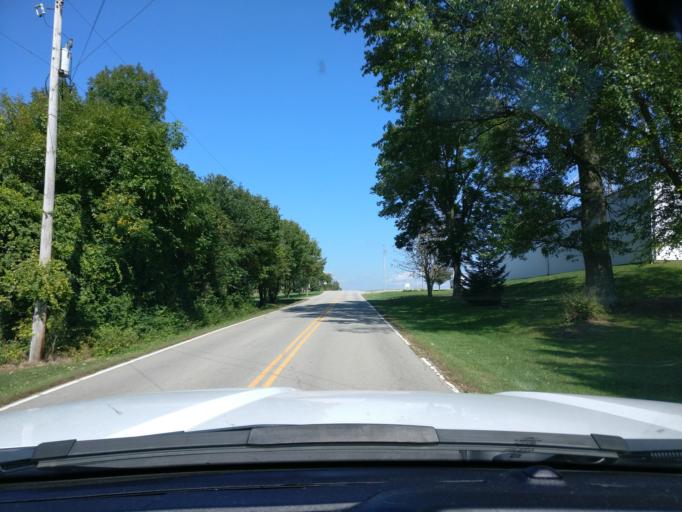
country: US
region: Ohio
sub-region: Warren County
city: Waynesville
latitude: 39.4789
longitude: -83.9930
